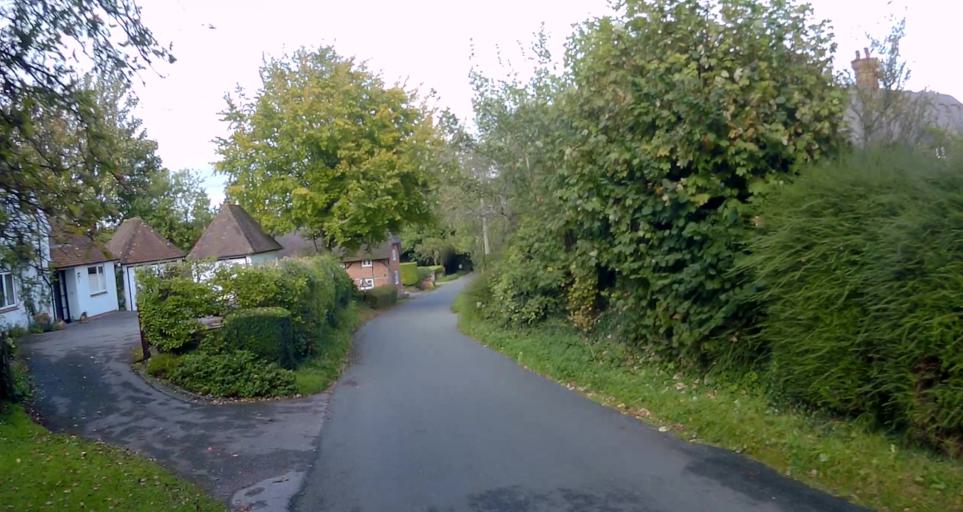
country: GB
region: England
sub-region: Hampshire
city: Kings Worthy
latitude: 51.0820
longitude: -1.2008
